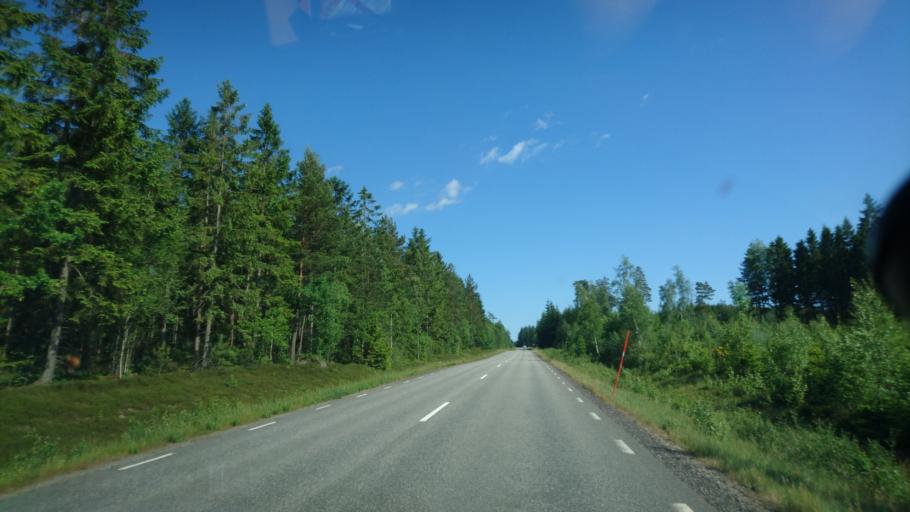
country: SE
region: Skane
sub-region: Osby Kommun
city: Lonsboda
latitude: 56.4361
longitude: 14.2539
